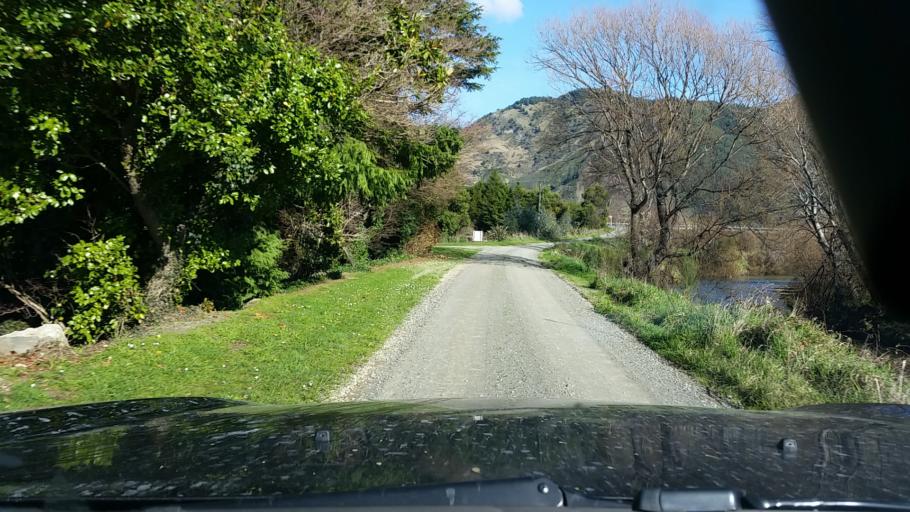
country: NZ
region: Marlborough
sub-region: Marlborough District
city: Picton
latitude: -41.3341
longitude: 173.7651
